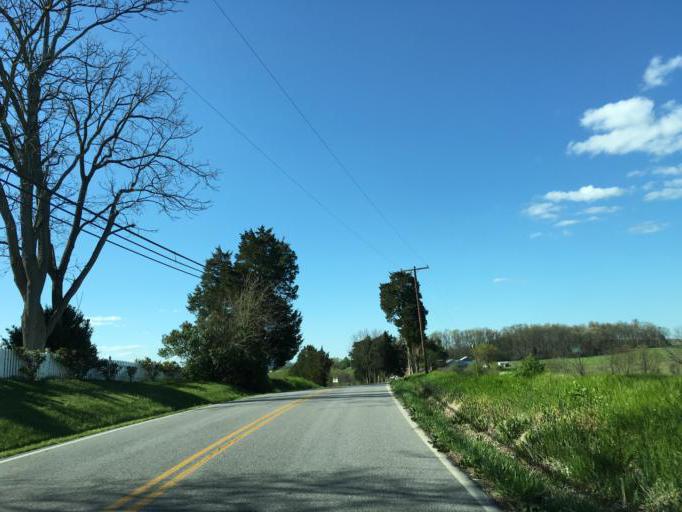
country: US
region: Maryland
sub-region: Frederick County
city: Emmitsburg
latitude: 39.6762
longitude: -77.3084
